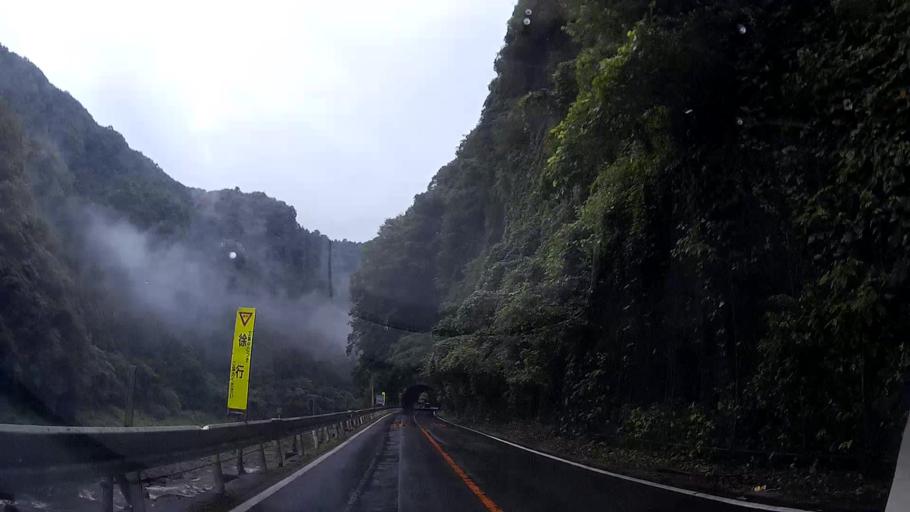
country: JP
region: Oita
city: Hita
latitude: 33.1795
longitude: 131.0174
